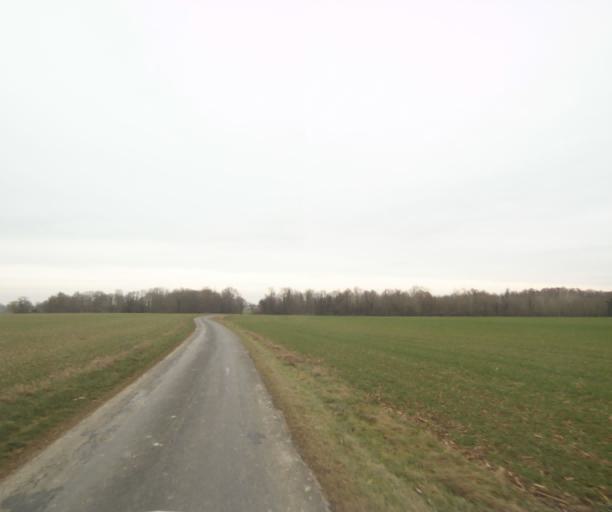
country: FR
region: Champagne-Ardenne
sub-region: Departement de la Haute-Marne
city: Villiers-en-Lieu
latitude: 48.6363
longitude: 4.8060
